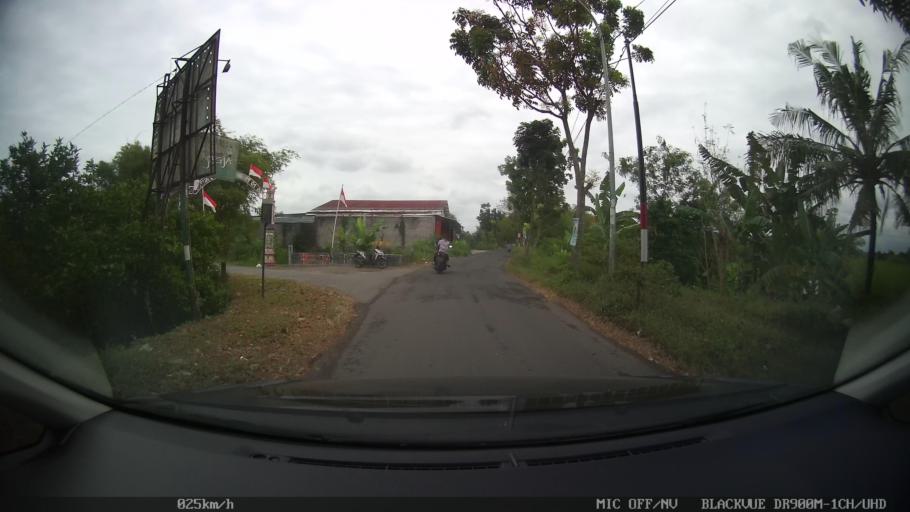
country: ID
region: Daerah Istimewa Yogyakarta
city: Sewon
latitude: -7.8512
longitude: 110.3949
